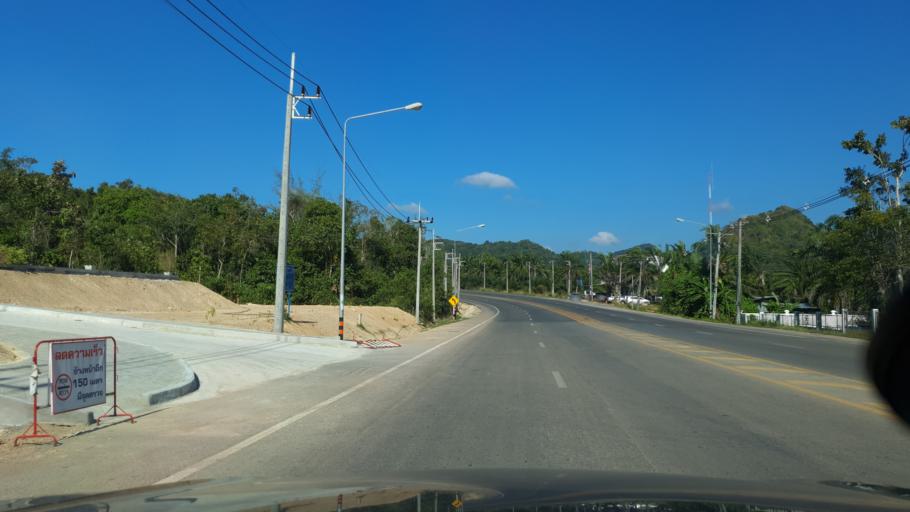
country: TH
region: Phangnga
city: Ban Ao Nang
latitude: 8.0411
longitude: 98.8489
